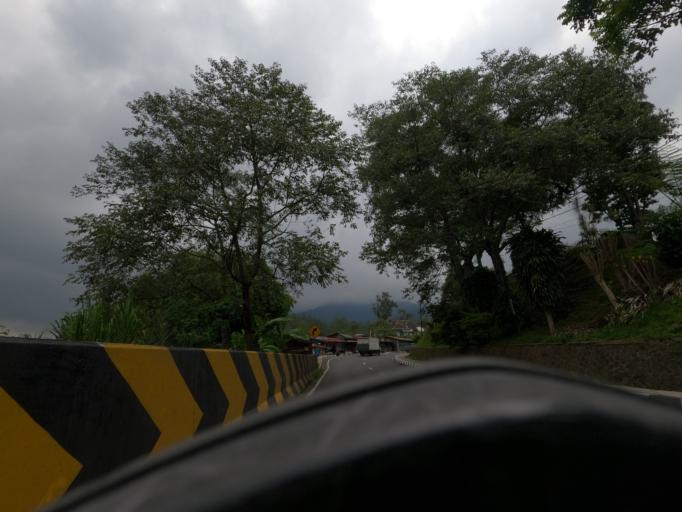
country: ID
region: West Java
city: Caringin
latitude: -6.7113
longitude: 107.0007
